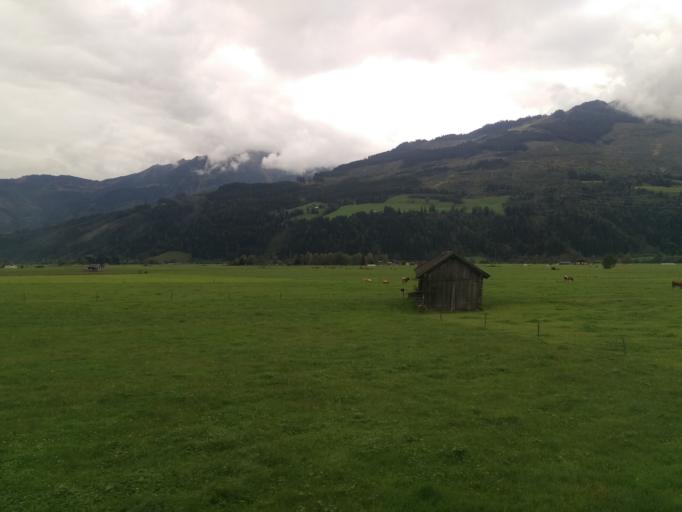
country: AT
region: Salzburg
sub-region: Politischer Bezirk Zell am See
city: Piesendorf
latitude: 47.2900
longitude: 12.7046
